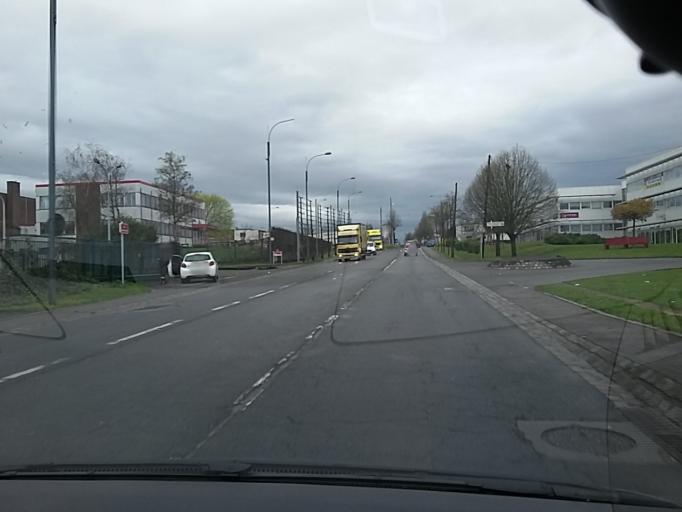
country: FR
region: Picardie
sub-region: Departement de la Somme
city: Amiens
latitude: 49.9309
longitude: 2.2781
